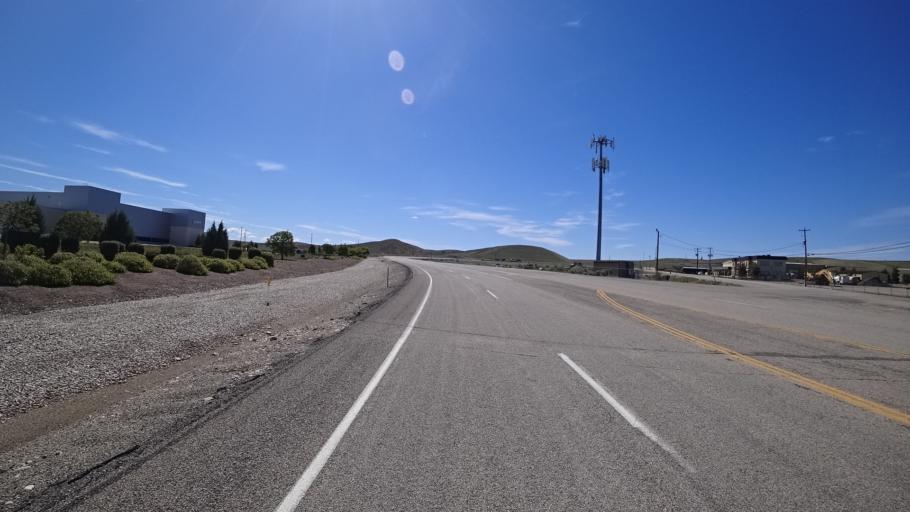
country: US
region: Idaho
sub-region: Ada County
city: Boise
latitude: 43.5121
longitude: -116.1425
